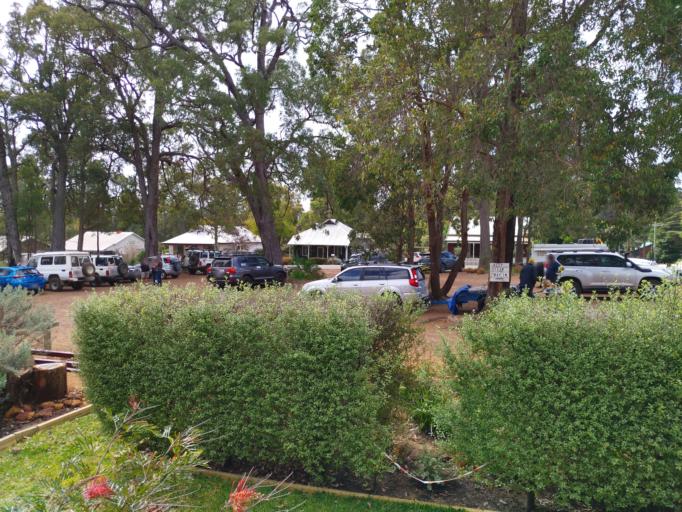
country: AU
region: Western Australia
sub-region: Serpentine-Jarrahdale
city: Byford
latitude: -32.2210
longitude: 116.0079
